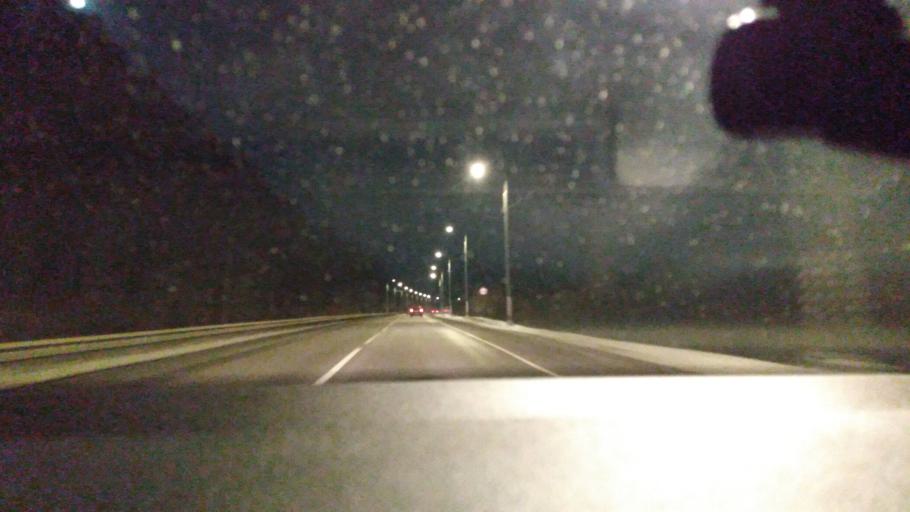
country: RU
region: Moskovskaya
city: Yegor'yevsk
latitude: 55.4500
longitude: 39.0056
